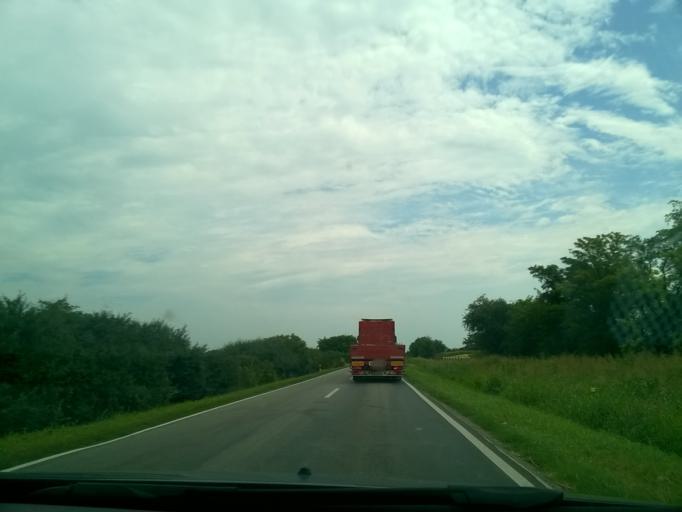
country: RS
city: Klek
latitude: 45.3849
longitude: 20.4621
